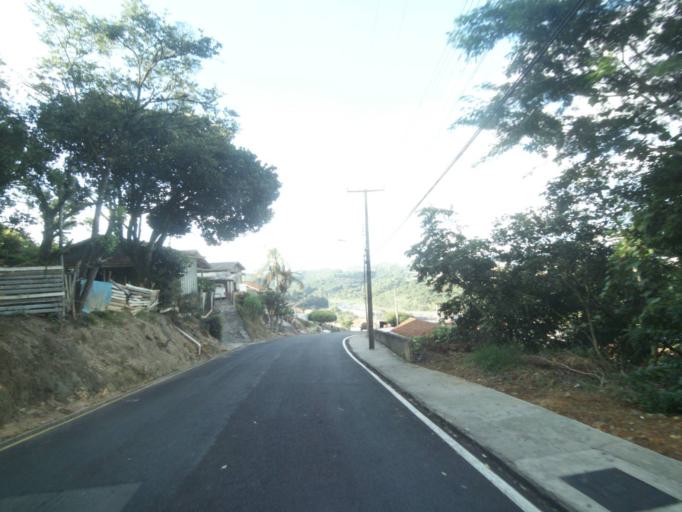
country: BR
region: Parana
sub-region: Telemaco Borba
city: Telemaco Borba
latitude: -24.3256
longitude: -50.6129
